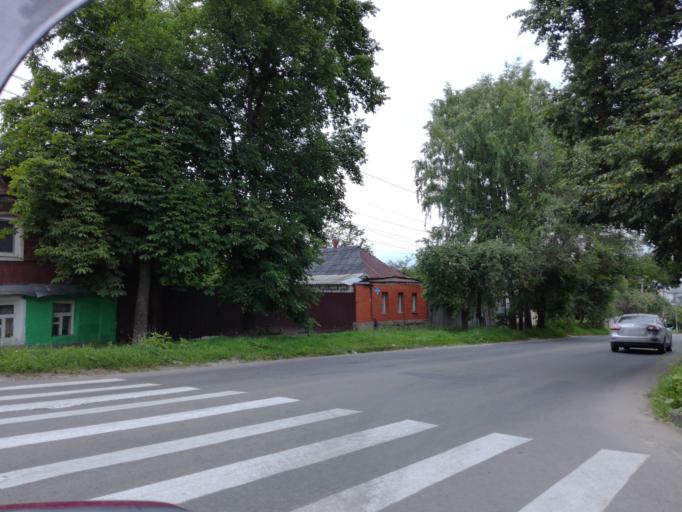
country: RU
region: Kursk
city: Kursk
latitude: 51.7262
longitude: 36.1667
